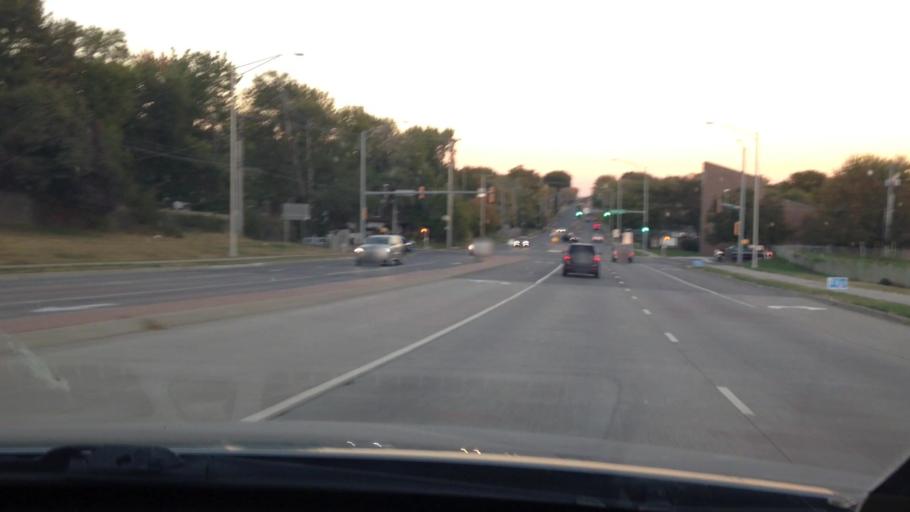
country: US
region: Kansas
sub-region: Johnson County
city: Lenexa
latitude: 38.9565
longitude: -94.7063
